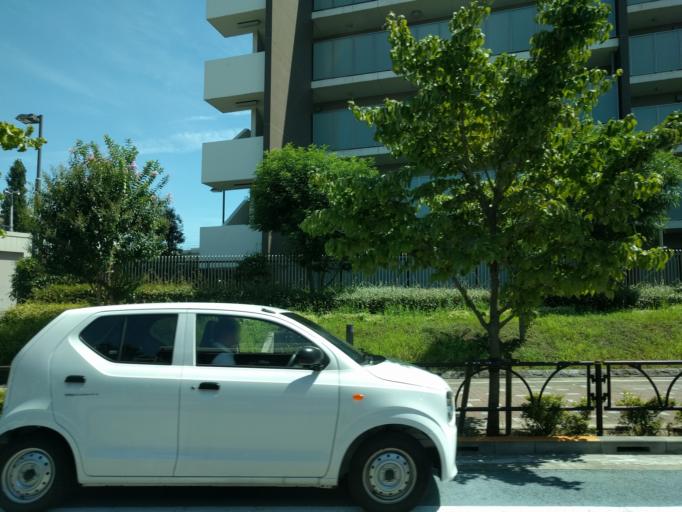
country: JP
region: Tokyo
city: Tokyo
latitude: 35.6533
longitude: 139.6408
